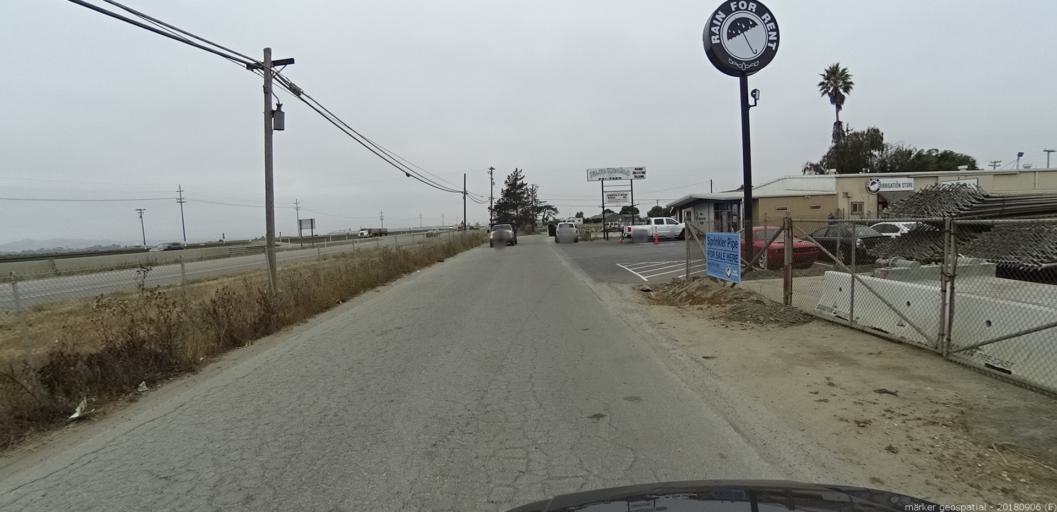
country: US
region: California
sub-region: Monterey County
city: Chualar
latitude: 36.6165
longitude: -121.5717
